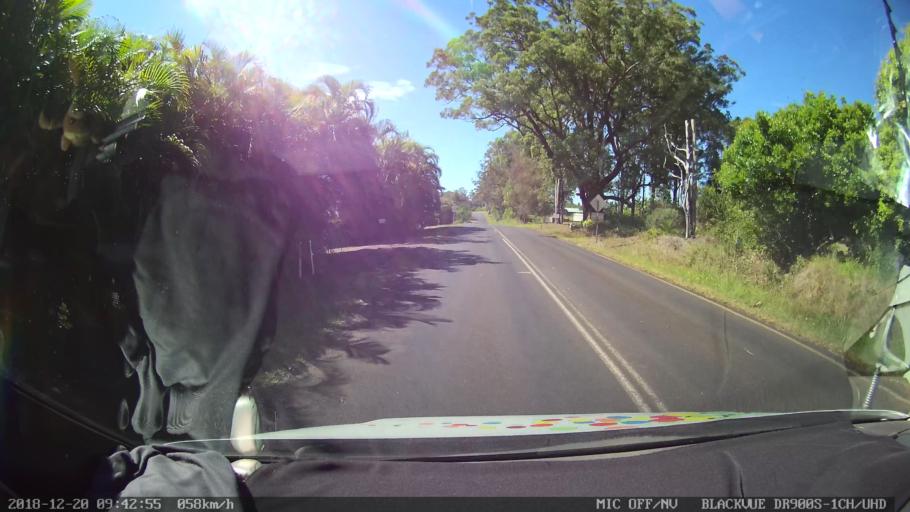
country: AU
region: New South Wales
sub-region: Lismore Municipality
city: Lismore
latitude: -28.7209
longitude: 153.2947
